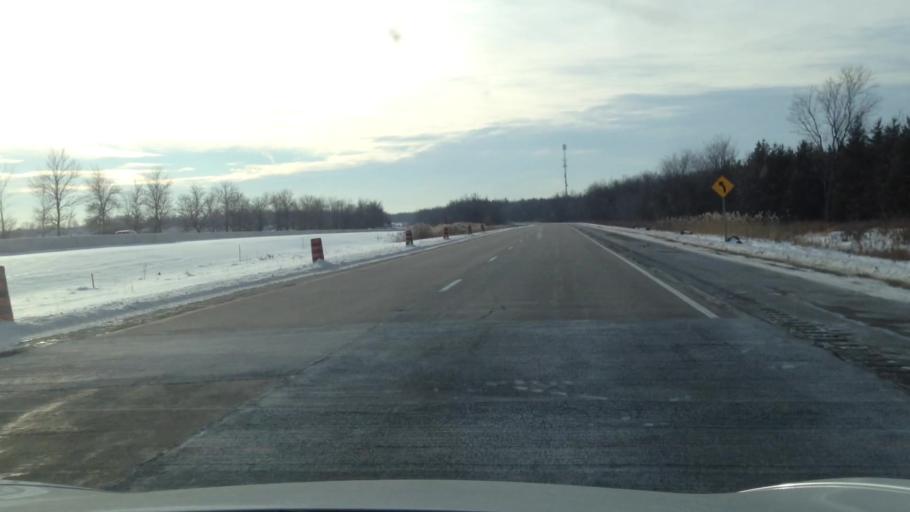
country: CA
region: Ontario
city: Hawkesbury
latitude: 45.5064
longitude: -74.5830
